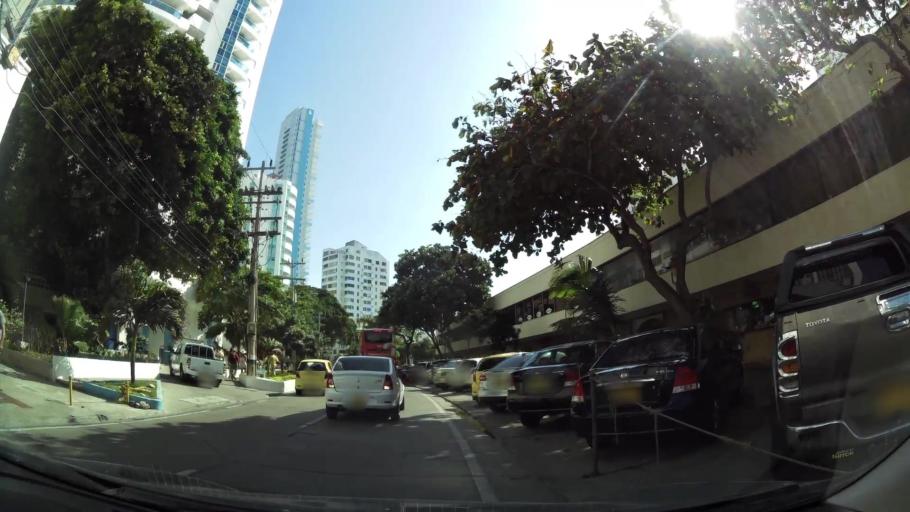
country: CO
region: Bolivar
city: Cartagena
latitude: 10.3970
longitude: -75.5630
